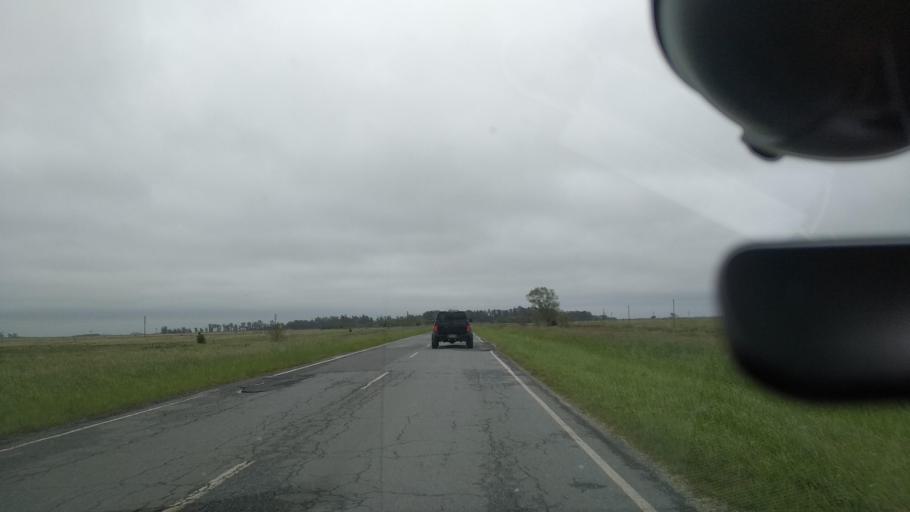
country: AR
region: Buenos Aires
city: Veronica
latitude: -35.5228
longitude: -57.3287
